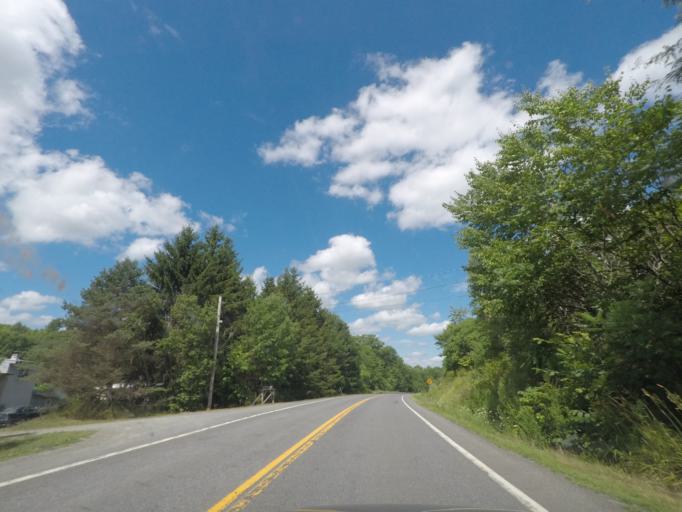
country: US
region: New York
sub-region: Rensselaer County
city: West Sand Lake
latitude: 42.6107
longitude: -73.6249
